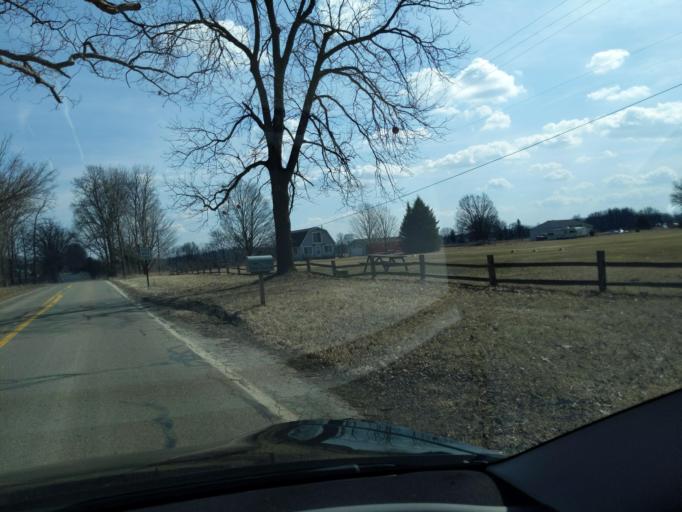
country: US
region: Michigan
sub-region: Ingham County
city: Stockbridge
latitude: 42.4459
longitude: -84.0652
